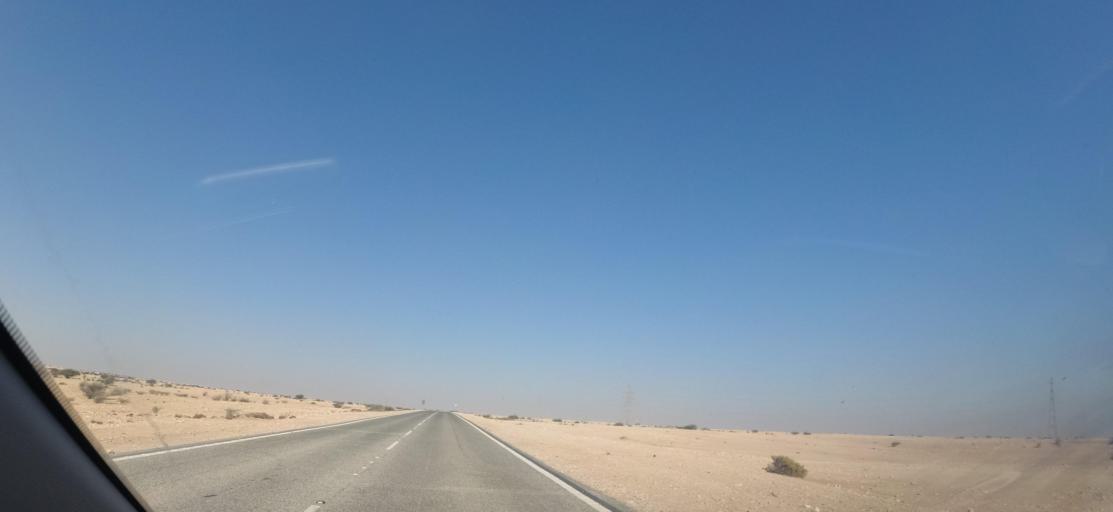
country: QA
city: Al Jumayliyah
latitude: 25.6305
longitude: 51.0953
